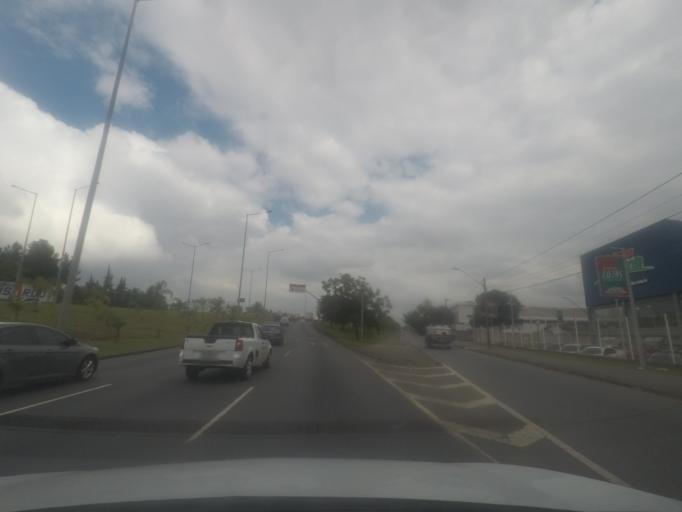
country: BR
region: Parana
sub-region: Curitiba
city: Curitiba
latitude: -25.4861
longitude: -49.2681
